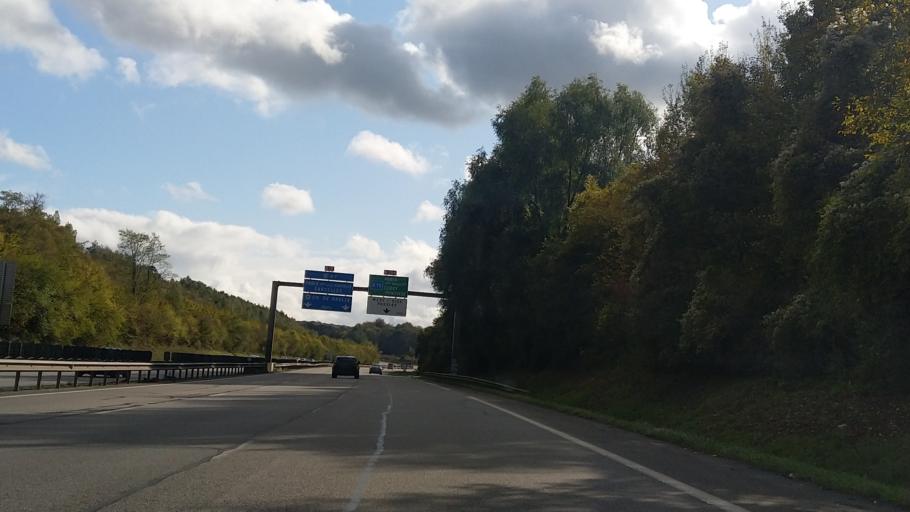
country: FR
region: Ile-de-France
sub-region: Departement du Val-d'Oise
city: Mours
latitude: 49.1145
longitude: 2.2533
